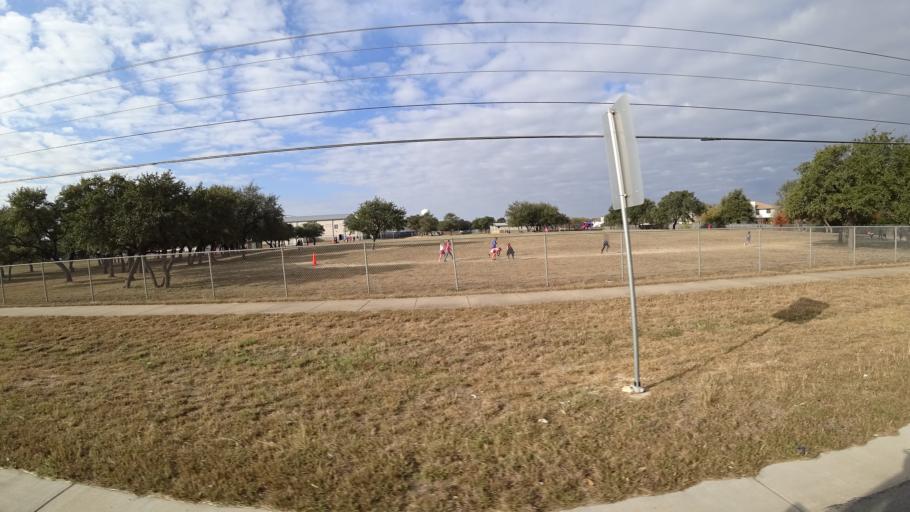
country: US
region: Texas
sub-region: Williamson County
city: Cedar Park
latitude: 30.5254
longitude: -97.8433
